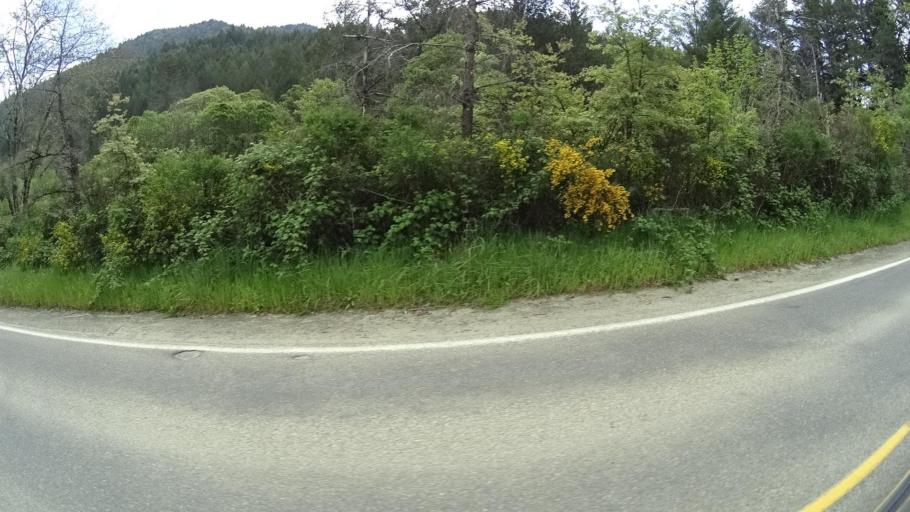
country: US
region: California
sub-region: Humboldt County
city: Redway
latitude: 40.1219
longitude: -123.8820
